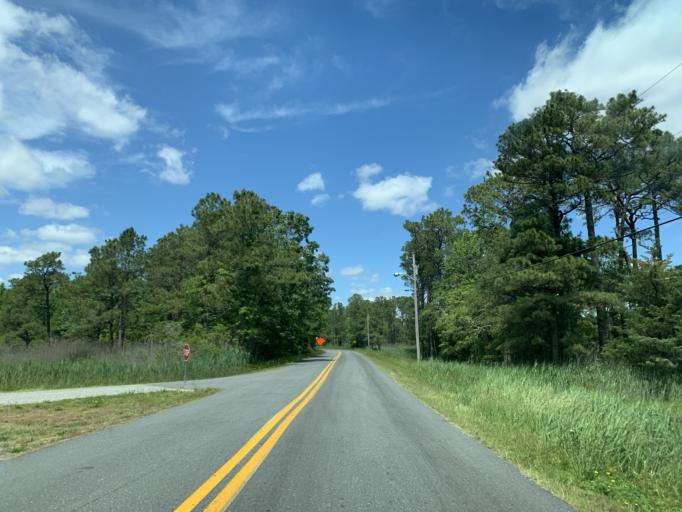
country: US
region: Maryland
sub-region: Worcester County
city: West Ocean City
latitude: 38.3125
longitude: -75.1187
